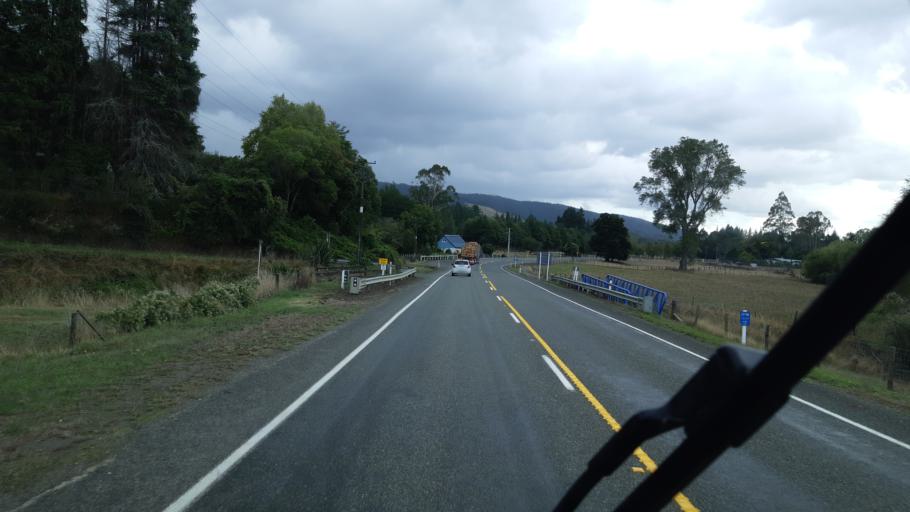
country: NZ
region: Tasman
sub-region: Tasman District
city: Wakefield
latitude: -41.4583
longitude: 172.9529
